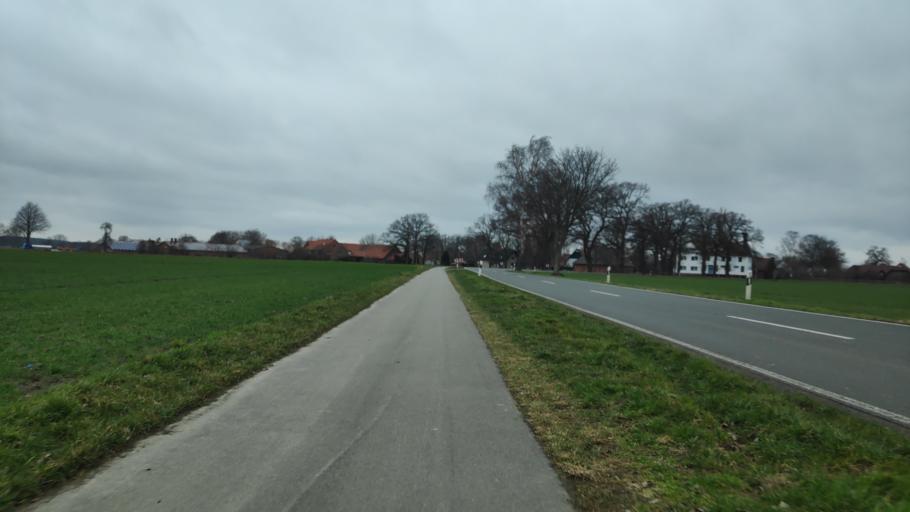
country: DE
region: North Rhine-Westphalia
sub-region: Regierungsbezirk Detmold
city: Hille
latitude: 52.3341
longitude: 8.8042
